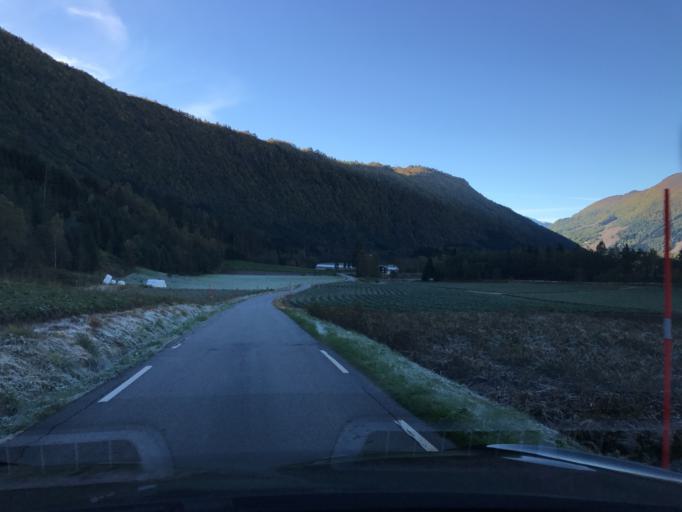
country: NO
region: More og Romsdal
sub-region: Norddal
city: Valldal
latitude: 62.3228
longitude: 7.3295
